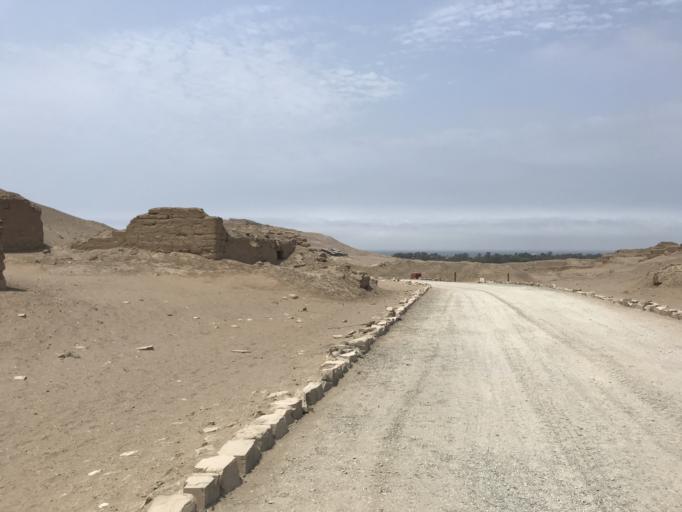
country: PE
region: Lima
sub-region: Lima
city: Punta Hermosa
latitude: -12.2561
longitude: -76.8969
